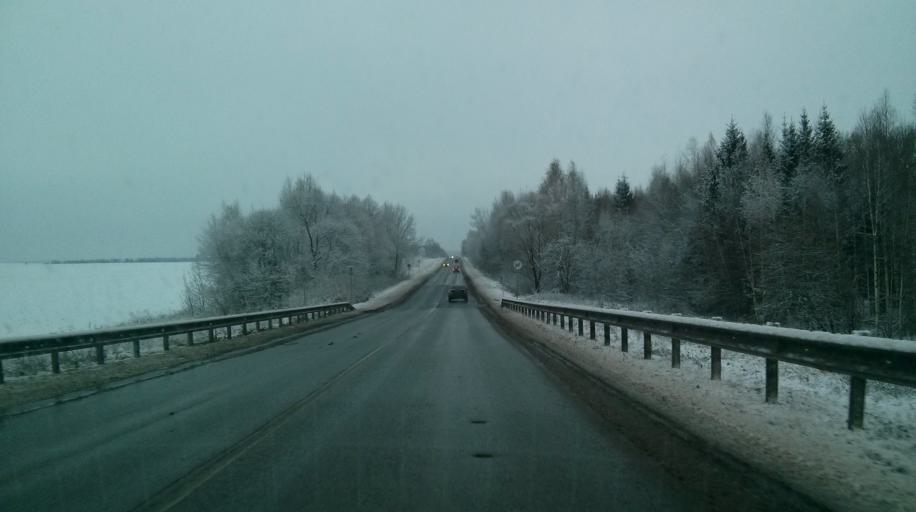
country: RU
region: Nizjnij Novgorod
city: Bogorodsk
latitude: 56.1124
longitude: 43.5910
